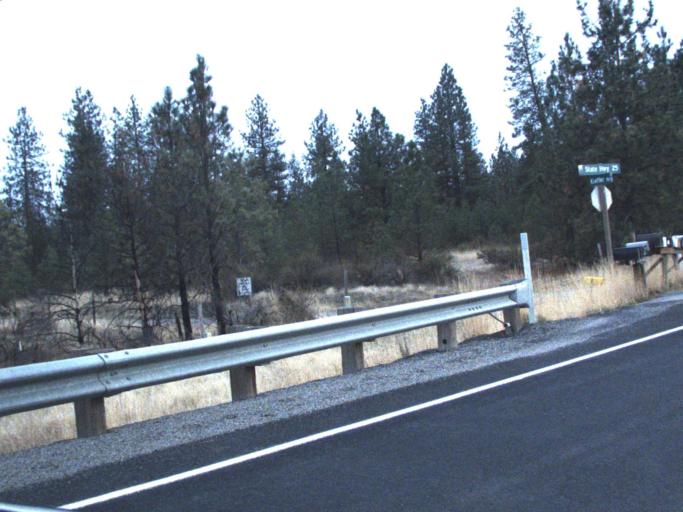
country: US
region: Washington
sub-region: Lincoln County
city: Davenport
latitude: 47.9164
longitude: -118.3310
